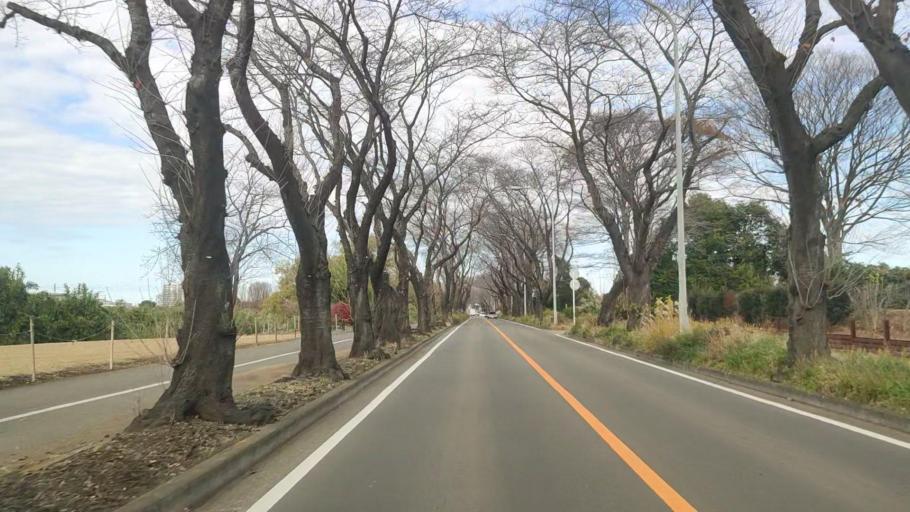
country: JP
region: Kanagawa
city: Minami-rinkan
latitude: 35.4851
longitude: 139.4804
